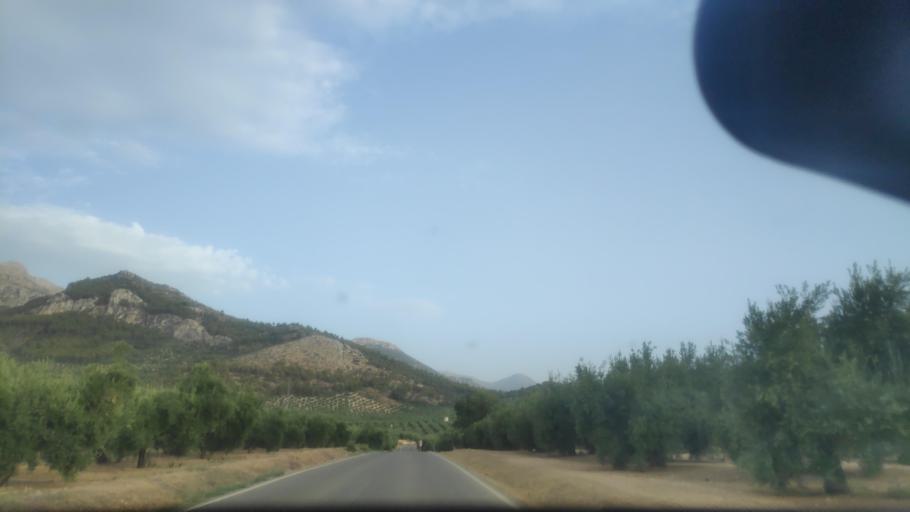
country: ES
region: Andalusia
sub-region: Provincia de Jaen
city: Jimena
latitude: 37.8332
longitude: -3.5276
